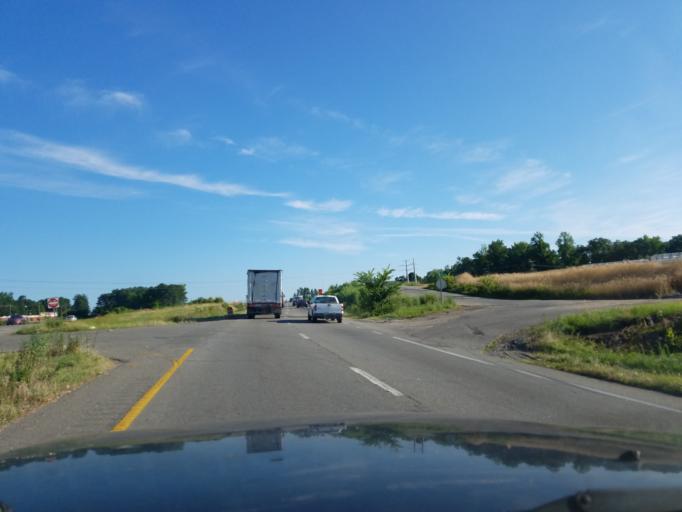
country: US
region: North Carolina
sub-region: Durham County
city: Durham
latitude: 35.9798
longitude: -78.8578
